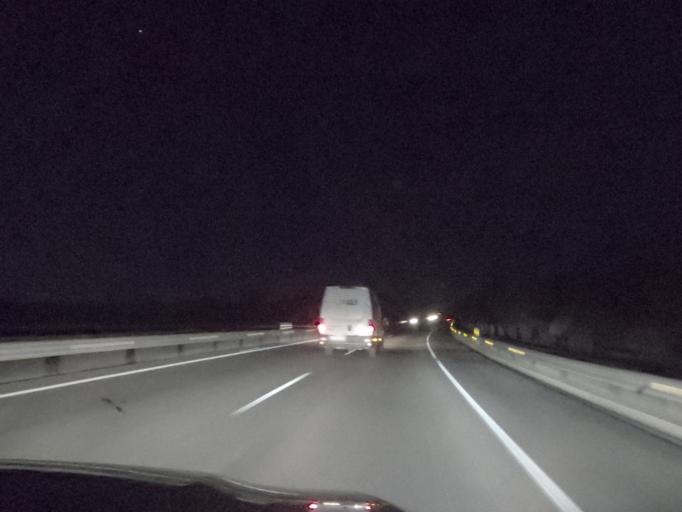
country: ES
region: Galicia
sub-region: Provincia de Ourense
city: Taboadela
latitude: 42.2312
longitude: -7.8462
